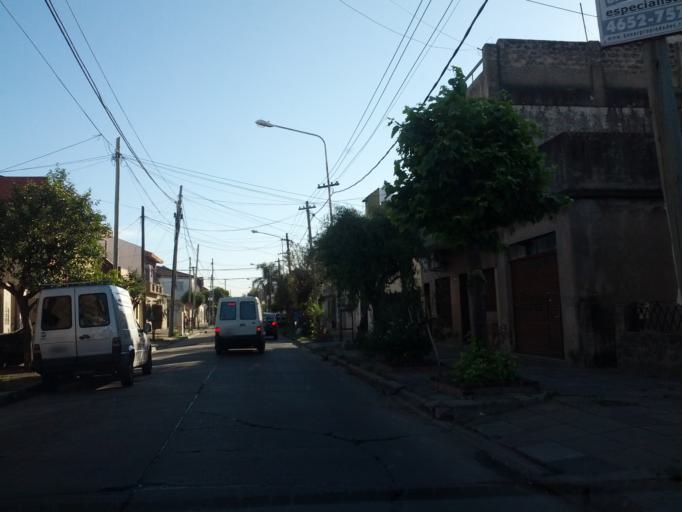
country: AR
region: Buenos Aires
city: San Justo
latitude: -34.6634
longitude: -58.5356
